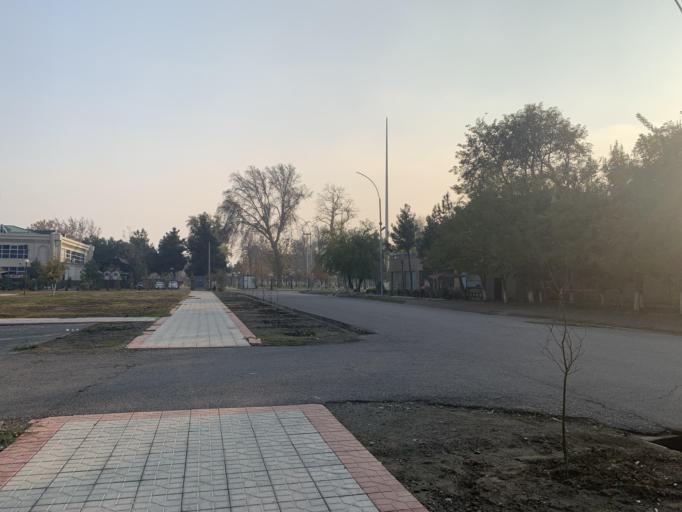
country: UZ
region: Fergana
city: Qo`qon
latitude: 40.5387
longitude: 70.9354
